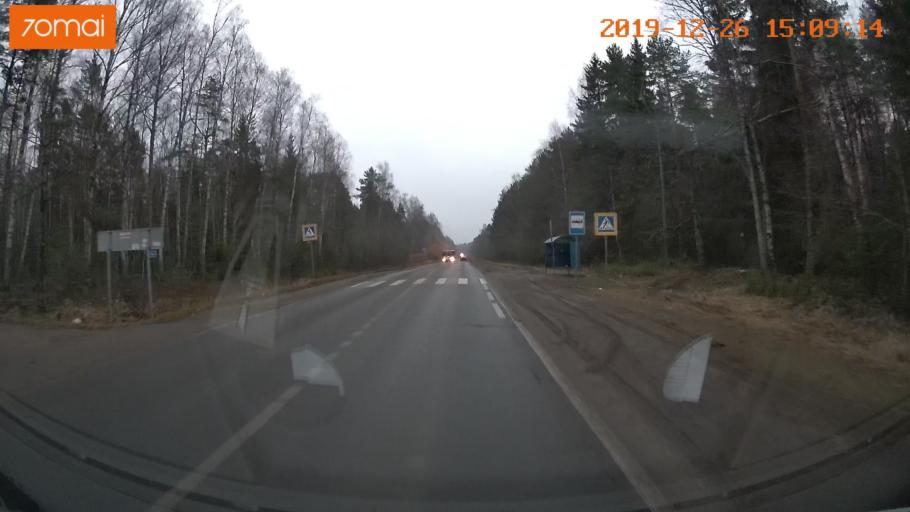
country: RU
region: Jaroslavl
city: Rybinsk
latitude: 58.1510
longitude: 38.8389
